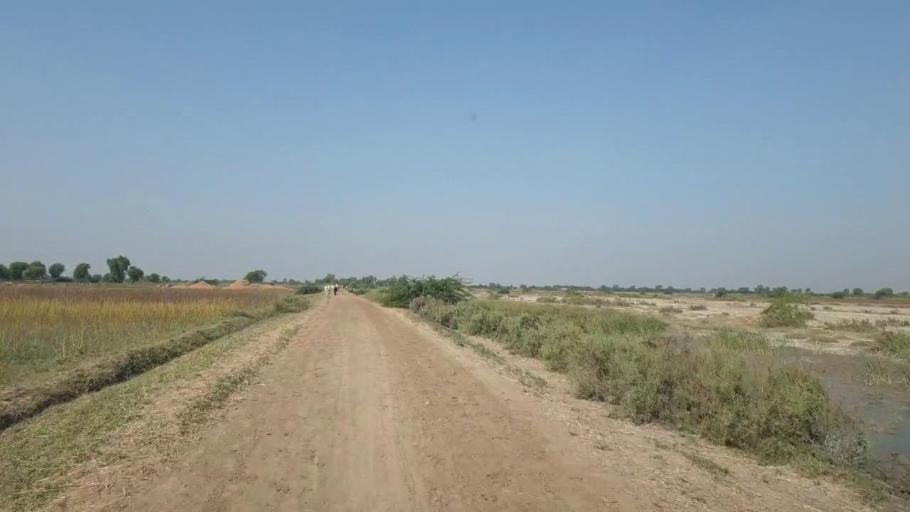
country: PK
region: Sindh
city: Badin
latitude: 24.5235
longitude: 68.7539
